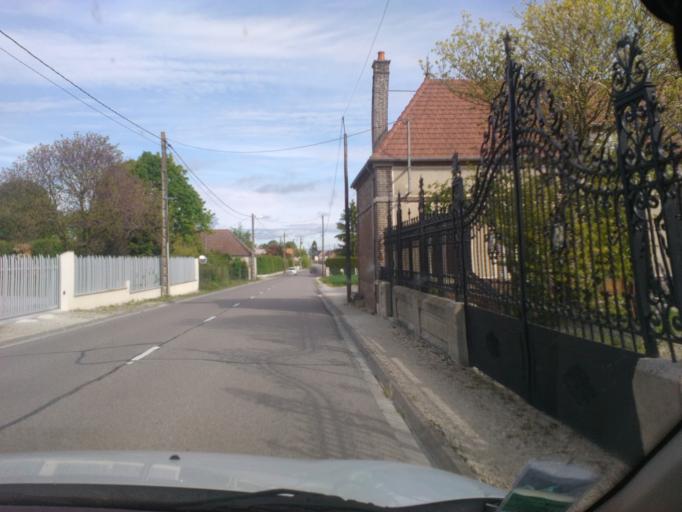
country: FR
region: Champagne-Ardenne
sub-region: Departement de l'Aube
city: Marigny-le-Chatel
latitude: 48.3883
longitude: 3.8320
